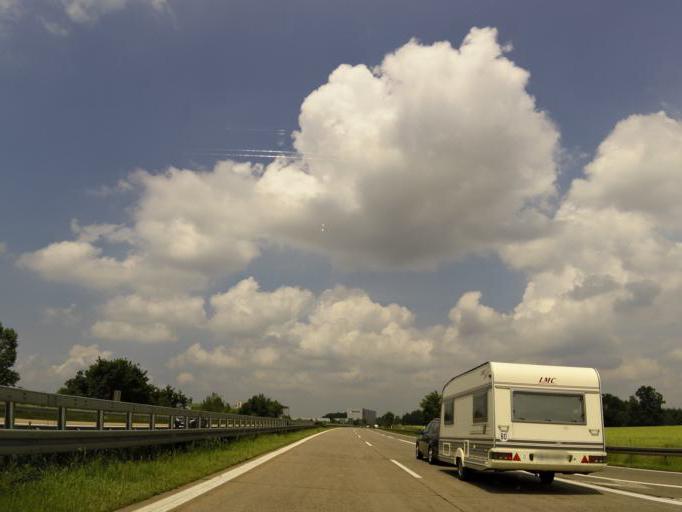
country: DE
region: Baden-Wuerttemberg
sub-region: Regierungsbezirk Stuttgart
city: Ellwangen
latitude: 48.9574
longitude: 10.1843
